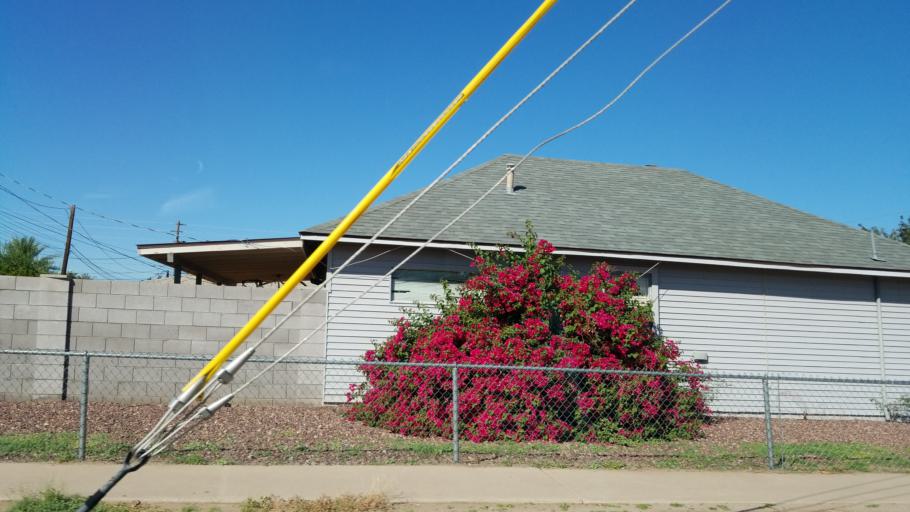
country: US
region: Arizona
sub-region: Maricopa County
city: Glendale
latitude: 33.5420
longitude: -112.1775
